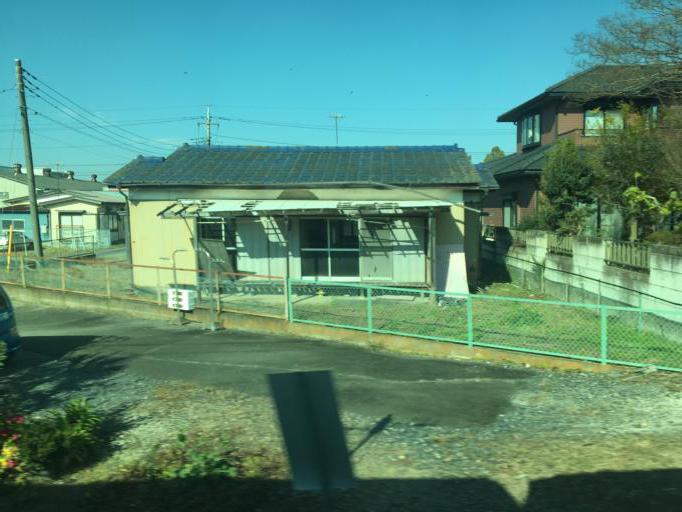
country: JP
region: Ibaraki
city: Yuki
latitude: 36.2969
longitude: 139.9256
